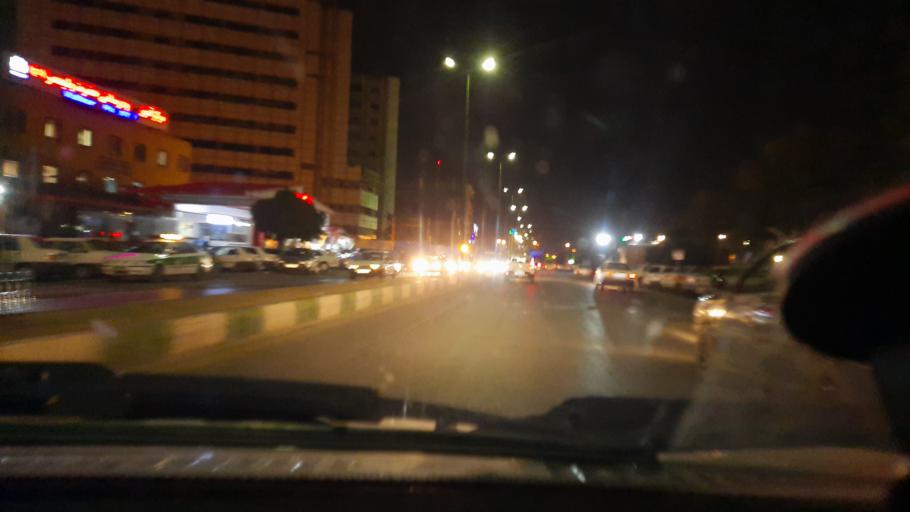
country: IR
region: Markazi
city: Arak
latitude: 34.0843
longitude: 49.7005
